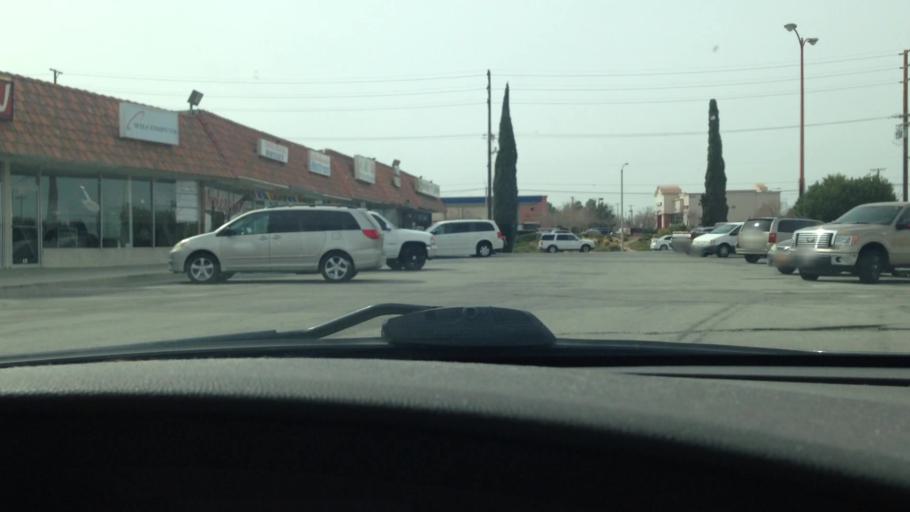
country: US
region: California
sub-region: Los Angeles County
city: Desert View Highlands
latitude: 34.5865
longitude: -118.1465
